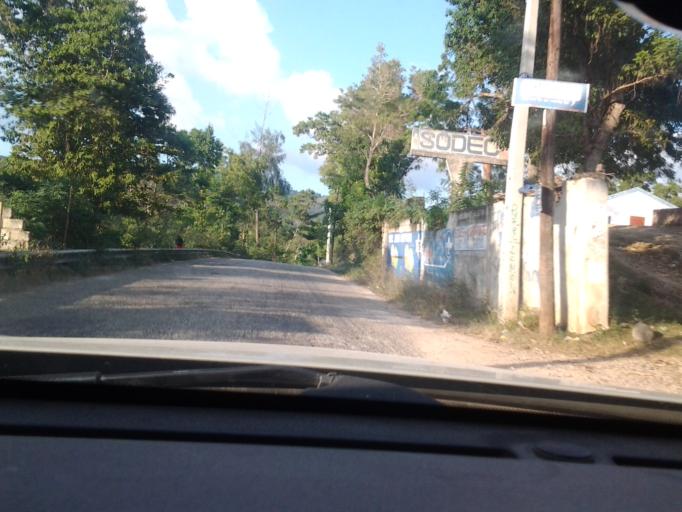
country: HT
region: Sud-Est
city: Jacmel
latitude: 18.3135
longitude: -72.5812
